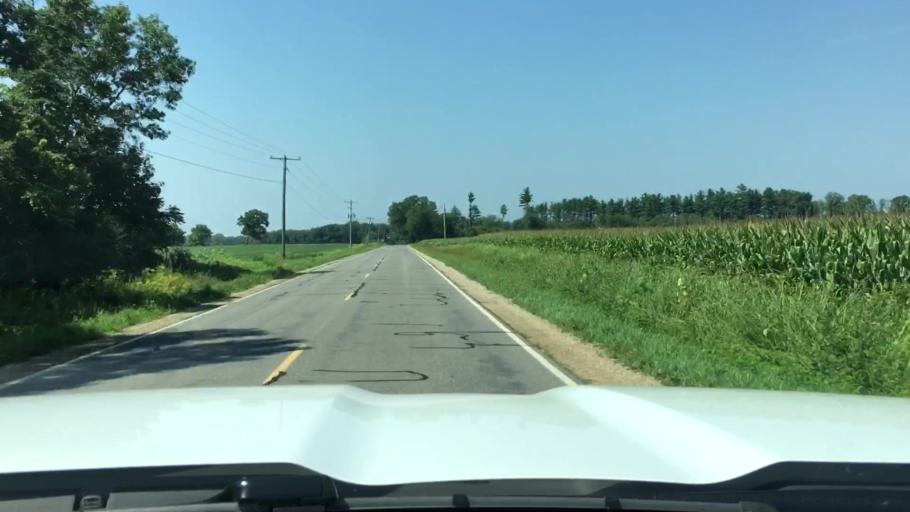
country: US
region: Michigan
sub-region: Saint Joseph County
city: Three Rivers
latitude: 41.9985
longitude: -85.5912
